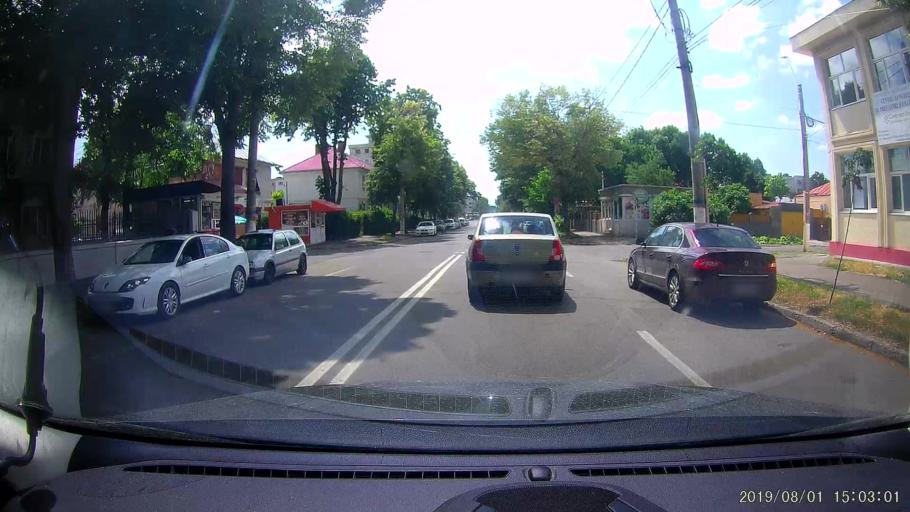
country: RO
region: Braila
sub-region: Municipiul Braila
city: Braila
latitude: 45.2665
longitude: 27.9611
